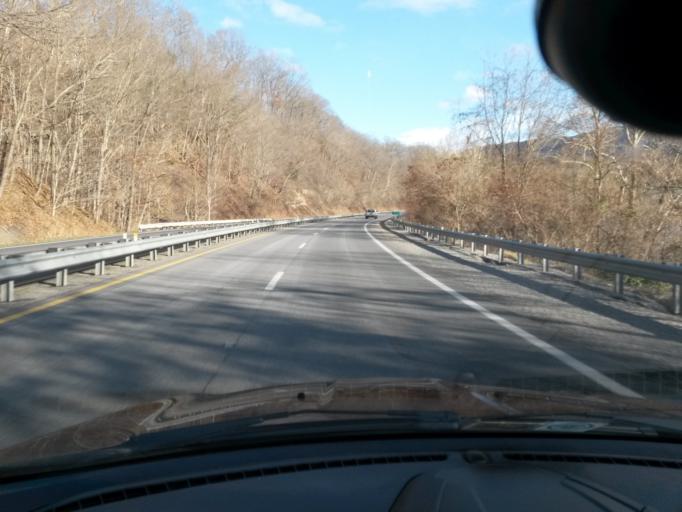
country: US
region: Virginia
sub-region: Giles County
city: Narrows
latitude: 37.3889
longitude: -80.8339
